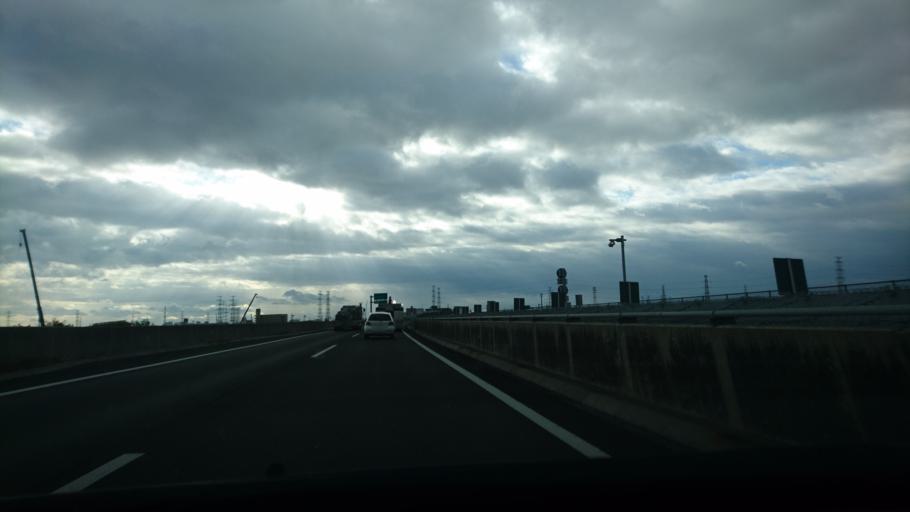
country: JP
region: Miyagi
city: Rifu
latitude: 38.2922
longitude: 140.9909
